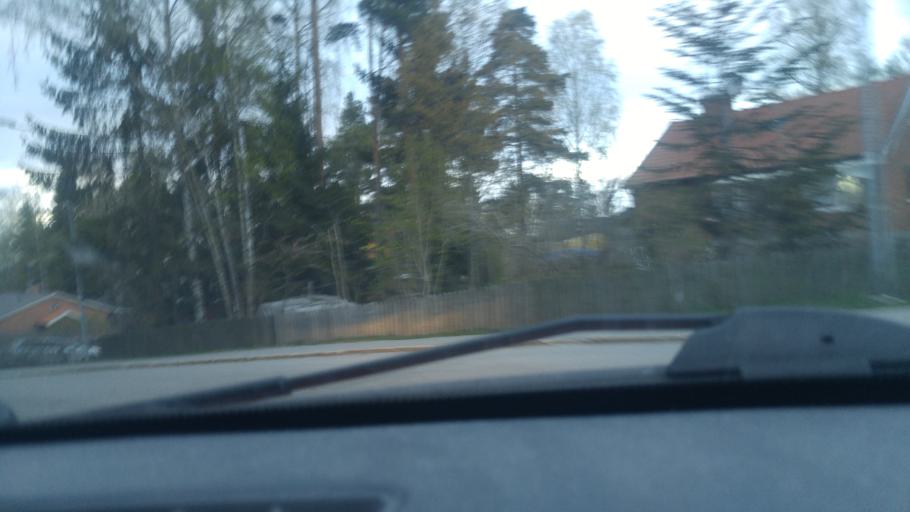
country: SE
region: Stockholm
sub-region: Upplands Vasby Kommun
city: Upplands Vaesby
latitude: 59.5084
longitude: 17.9352
